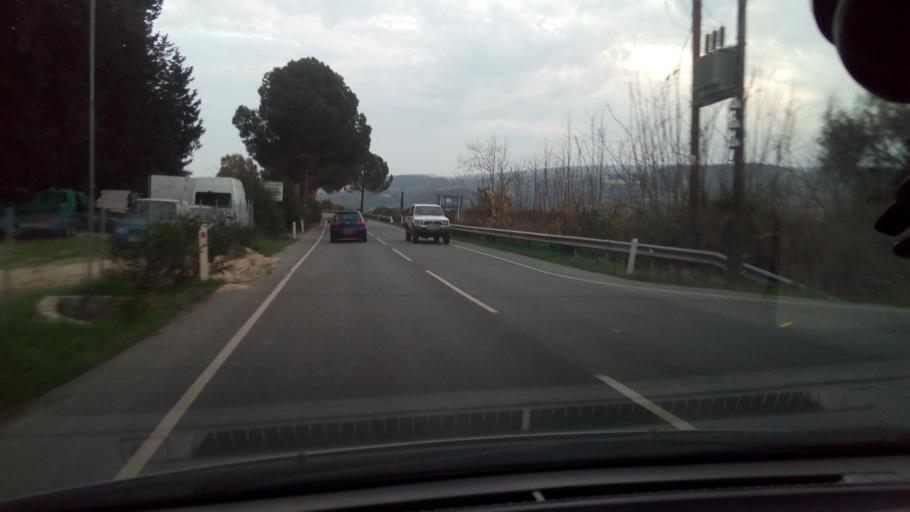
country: CY
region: Pafos
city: Polis
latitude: 35.0223
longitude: 32.4334
